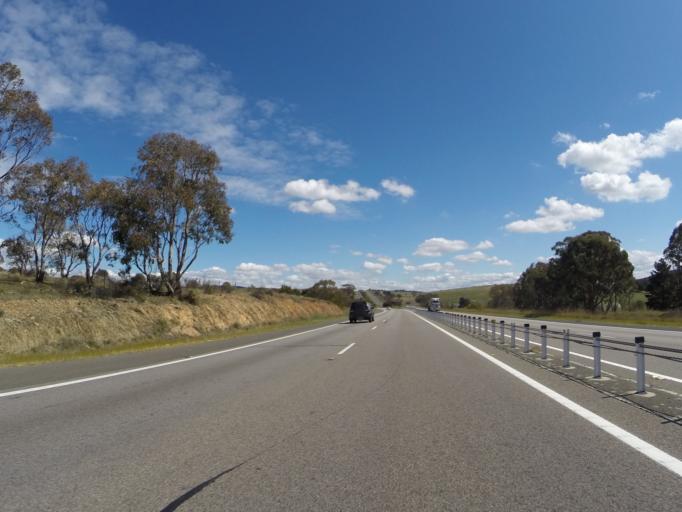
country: AU
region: New South Wales
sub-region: Goulburn Mulwaree
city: Goulburn
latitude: -34.7318
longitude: 149.8135
